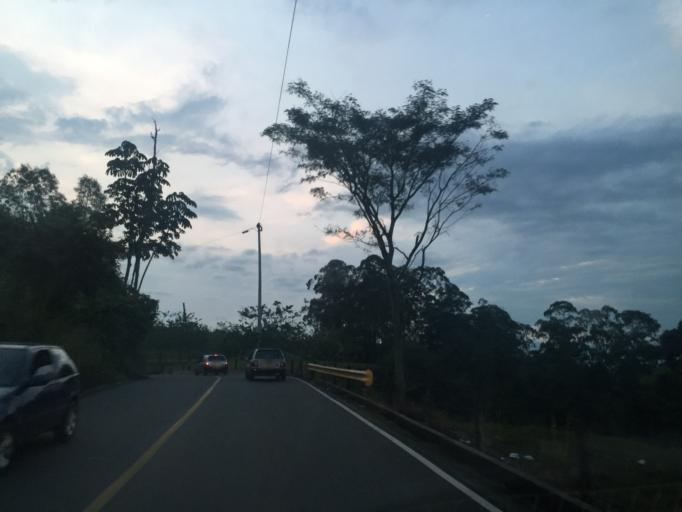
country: CO
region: Valle del Cauca
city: Ulloa
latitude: 4.7711
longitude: -75.7643
